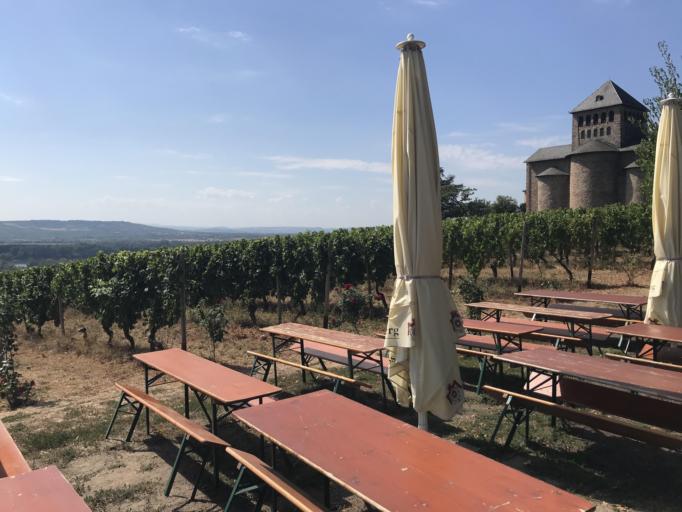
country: DE
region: Rheinland-Pfalz
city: Oestrich-Winkel
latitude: 50.0005
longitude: 7.9858
